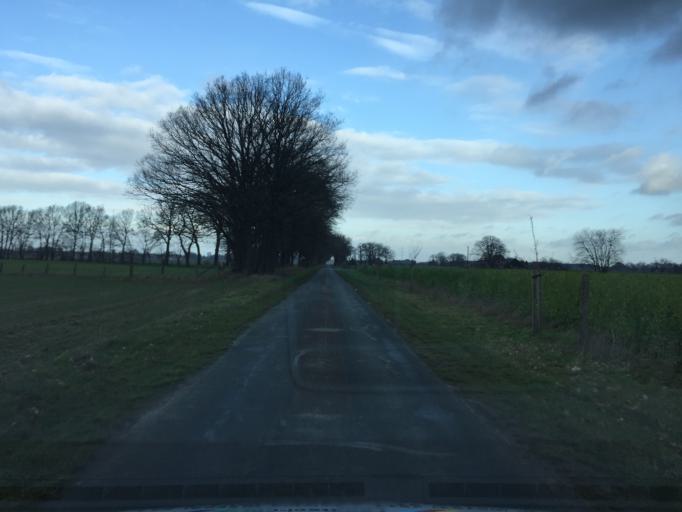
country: DE
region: Lower Saxony
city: Steyerberg
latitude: 52.5247
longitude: 9.0008
